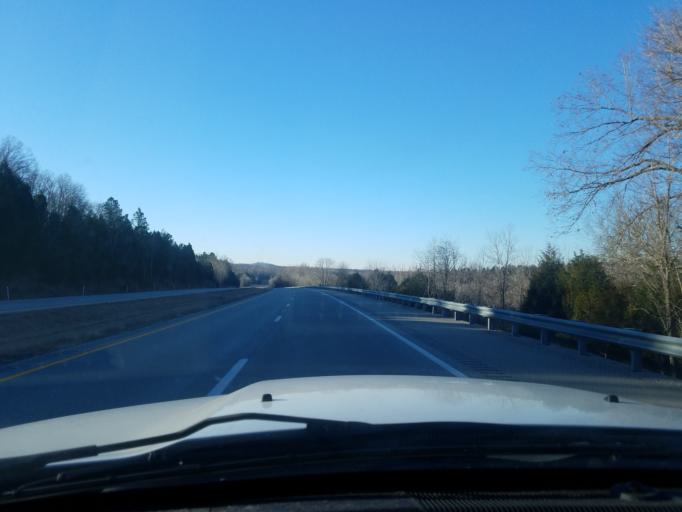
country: US
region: Kentucky
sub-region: Grayson County
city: Leitchfield
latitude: 37.4324
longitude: -86.3836
